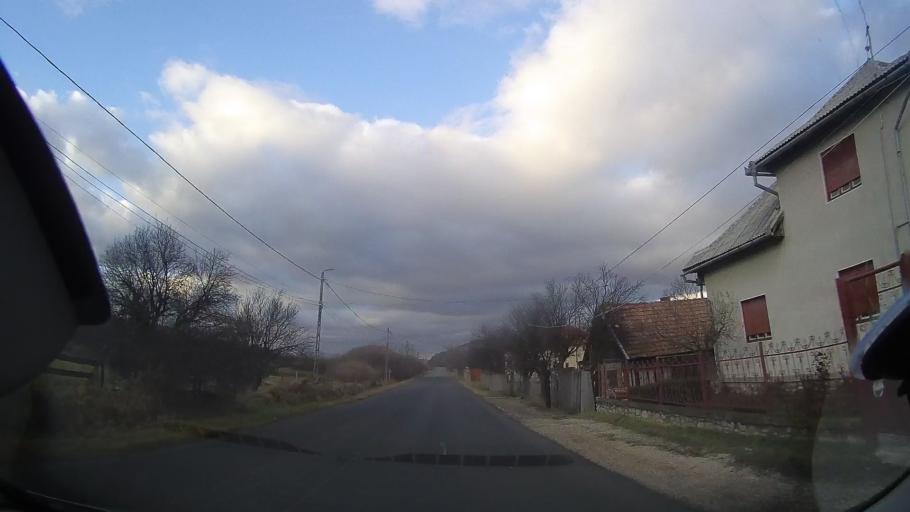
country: RO
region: Cluj
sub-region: Comuna Calatele
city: Calatele
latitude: 46.7766
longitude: 23.0067
